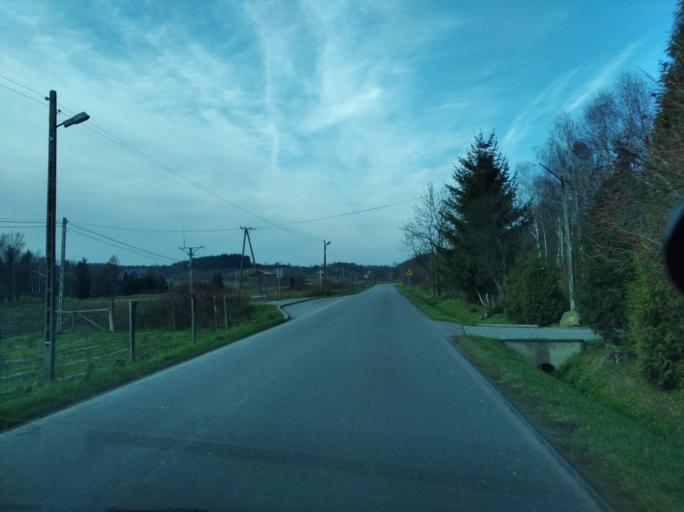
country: PL
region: Subcarpathian Voivodeship
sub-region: Powiat strzyzowski
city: Strzyzow
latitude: 49.8879
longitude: 21.7542
